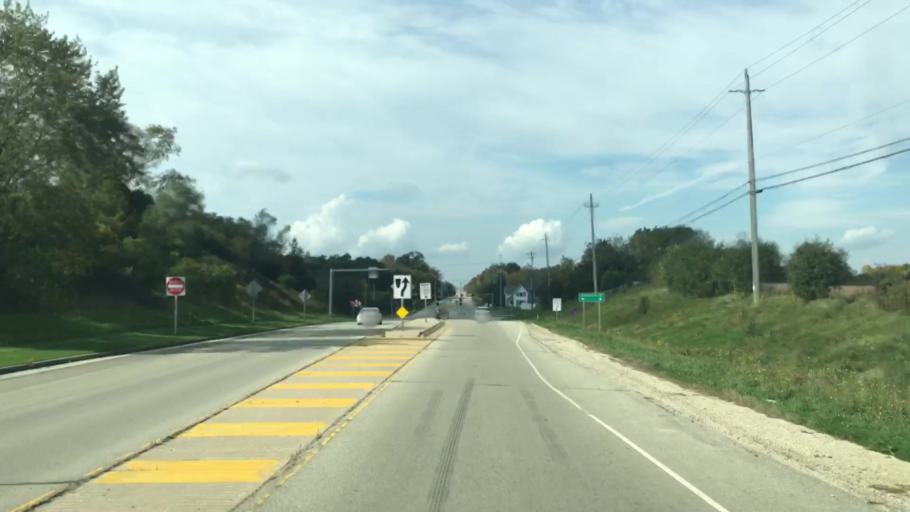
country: US
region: Wisconsin
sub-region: Ozaukee County
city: Mequon
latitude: 43.2214
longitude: -88.0408
